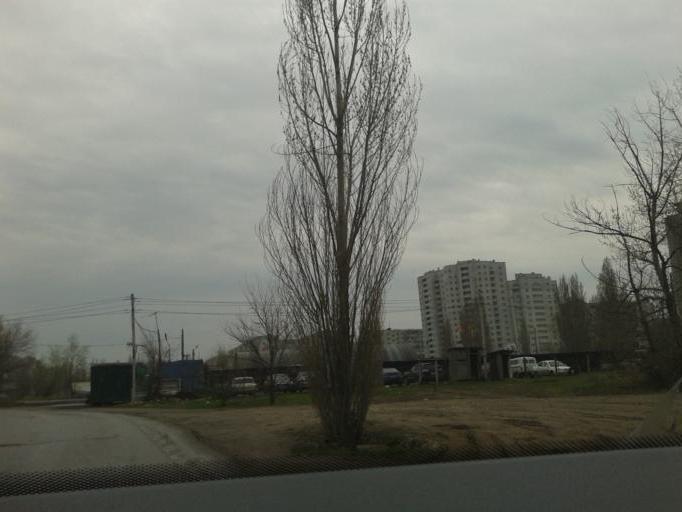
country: RU
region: Volgograd
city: Volgograd
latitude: 48.7610
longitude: 44.4983
